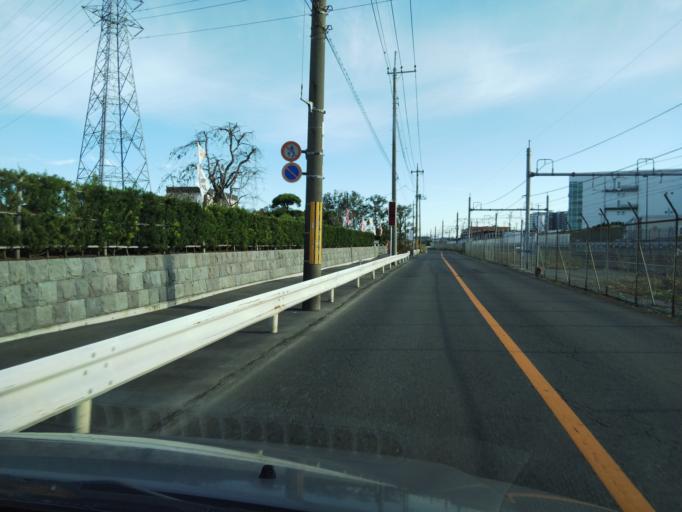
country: JP
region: Saitama
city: Yoshikawa
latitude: 35.8649
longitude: 139.8623
